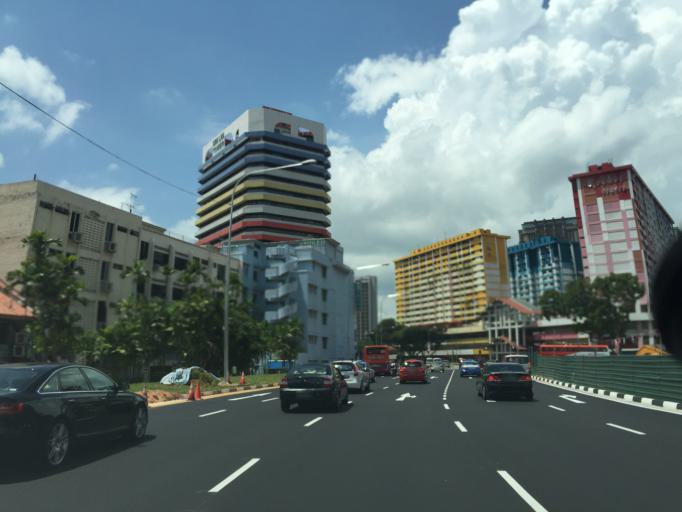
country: SG
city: Singapore
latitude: 1.3039
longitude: 103.8533
